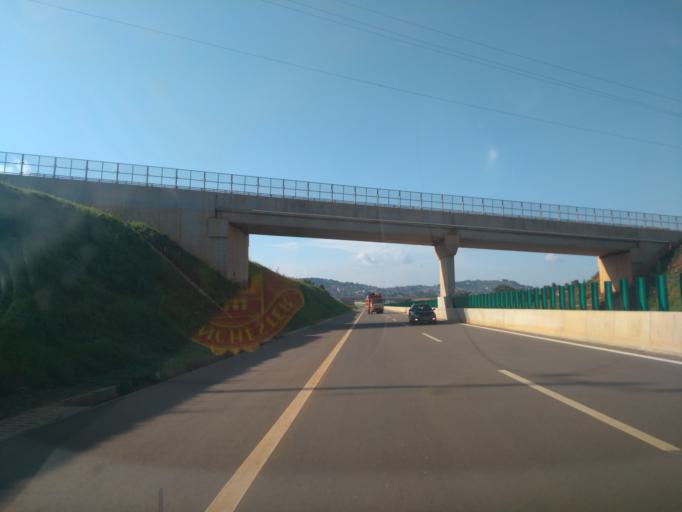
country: UG
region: Central Region
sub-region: Wakiso District
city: Kajansi
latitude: 0.2049
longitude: 32.5280
